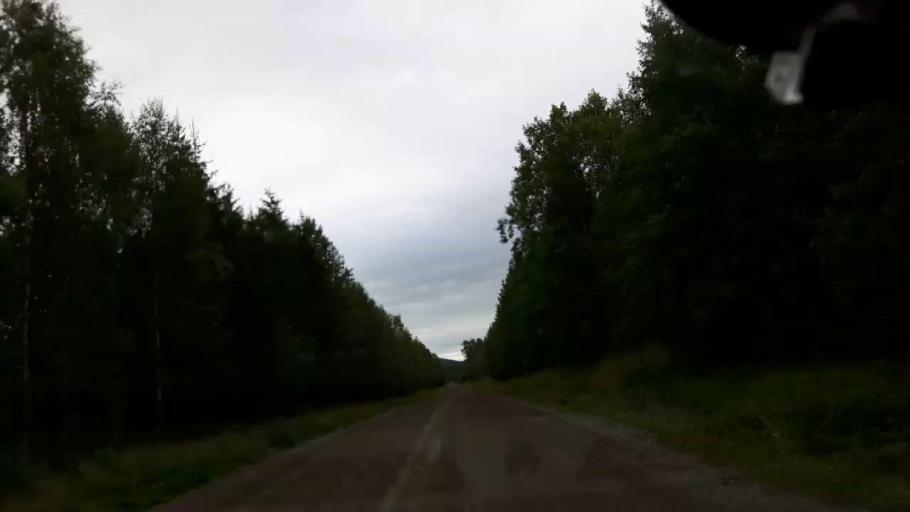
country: SE
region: Jaemtland
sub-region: Braecke Kommun
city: Braecke
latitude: 62.9017
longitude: 15.5985
